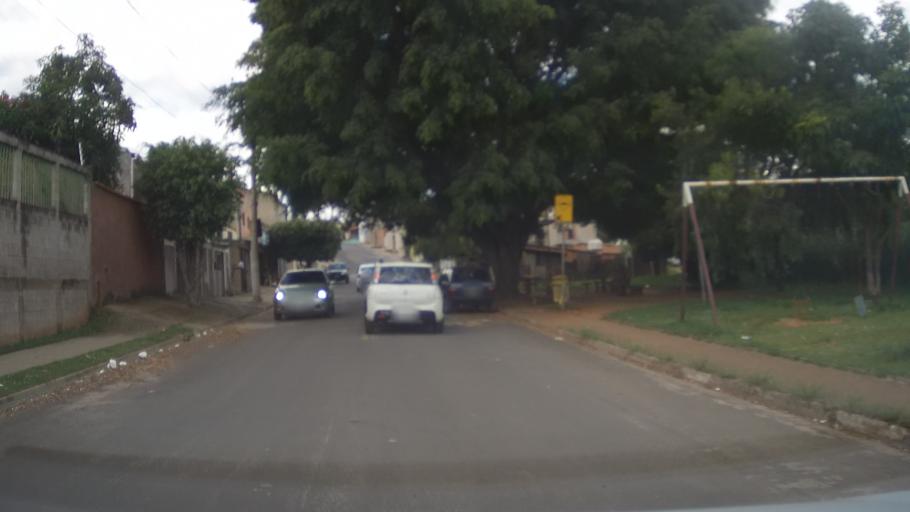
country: BR
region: Sao Paulo
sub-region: Campinas
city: Campinas
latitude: -22.9191
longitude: -47.0239
